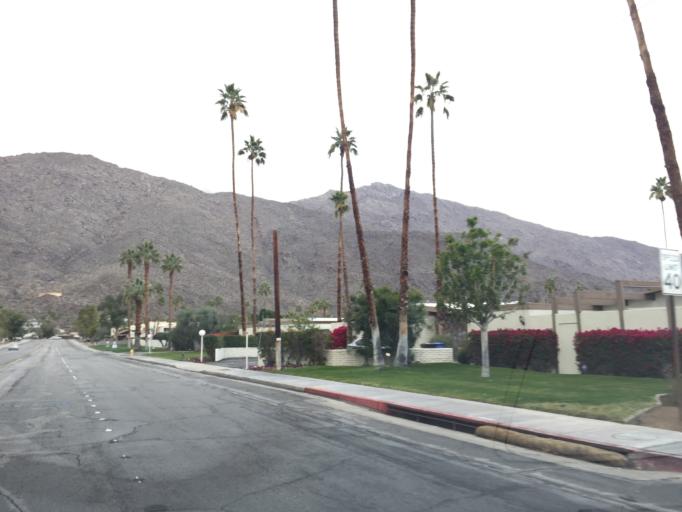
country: US
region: California
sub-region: Riverside County
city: Palm Springs
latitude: 33.7941
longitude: -116.5414
